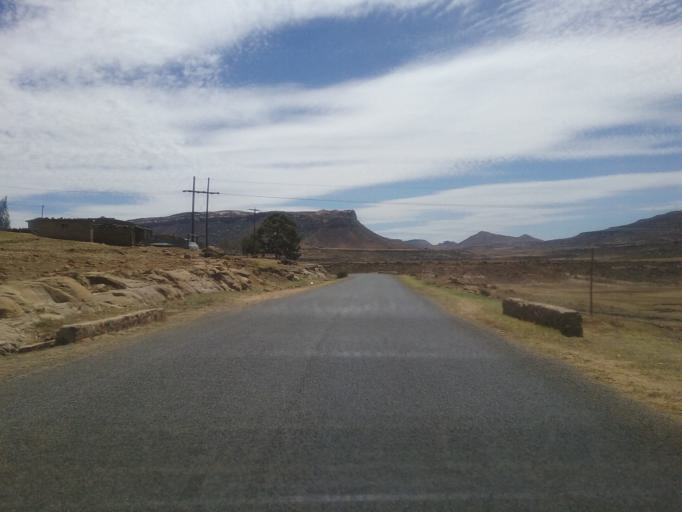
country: LS
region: Mafeteng
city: Mafeteng
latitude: -29.9079
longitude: 27.2502
